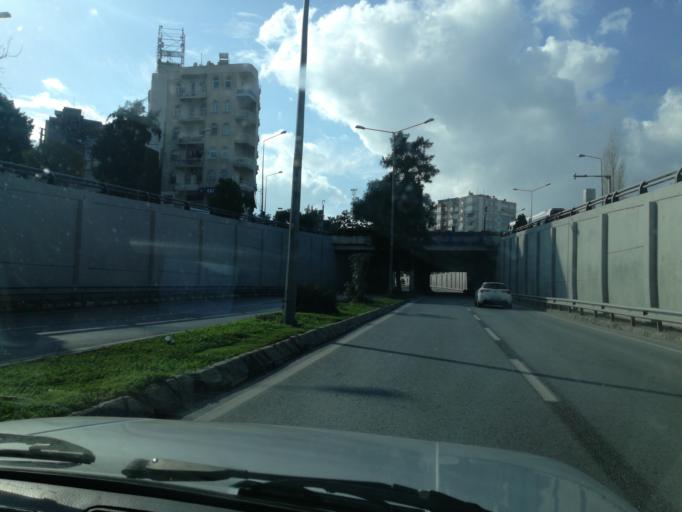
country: TR
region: Izmir
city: Izmir
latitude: 38.4113
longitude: 27.1297
